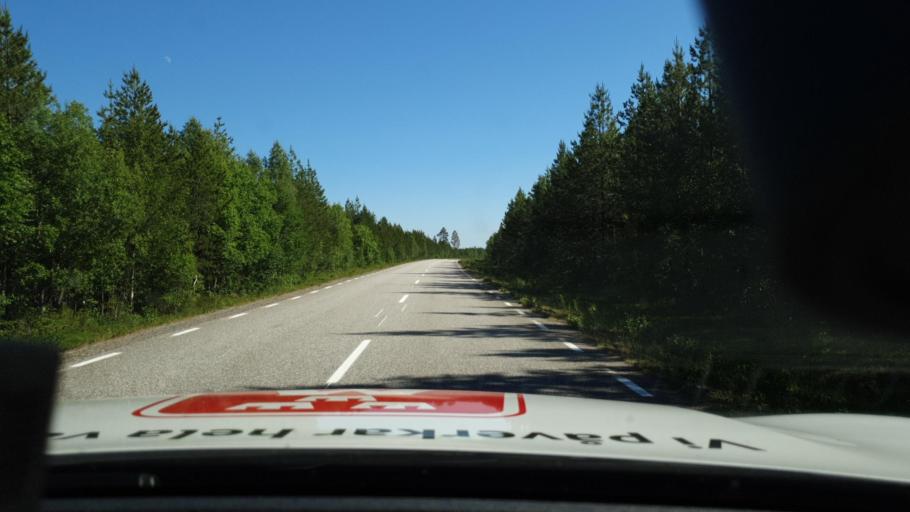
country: SE
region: Norrbotten
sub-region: Lulea Kommun
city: Ranea
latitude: 66.0019
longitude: 22.3266
